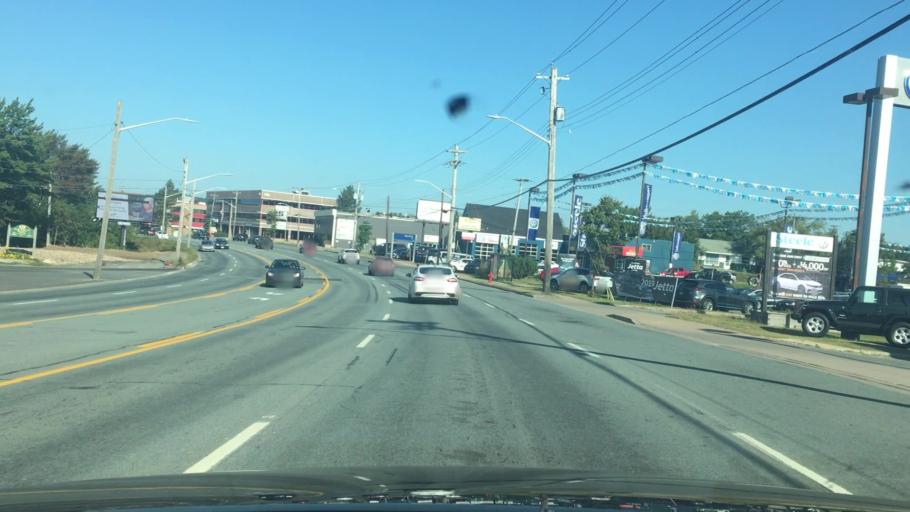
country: CA
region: Nova Scotia
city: Dartmouth
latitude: 44.7017
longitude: -63.6076
